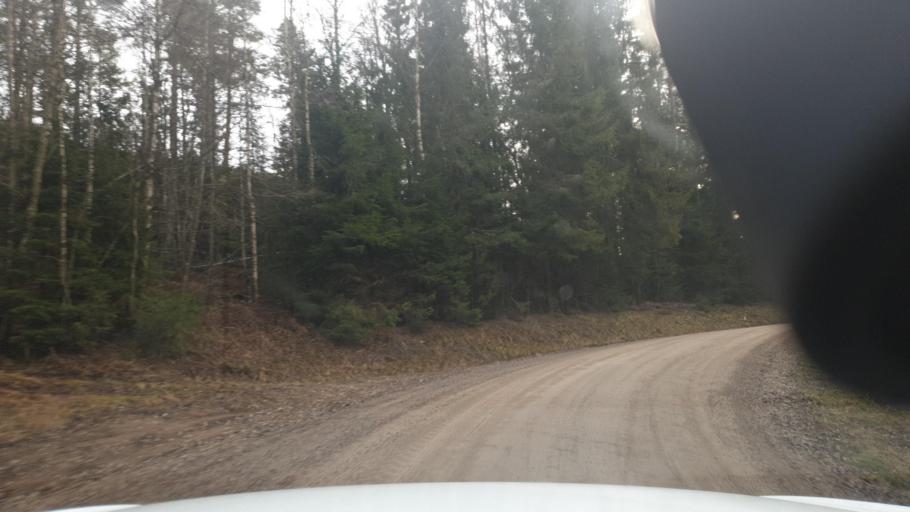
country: NO
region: Hedmark
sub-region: Eidskog
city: Skotterud
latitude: 59.7393
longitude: 12.0785
